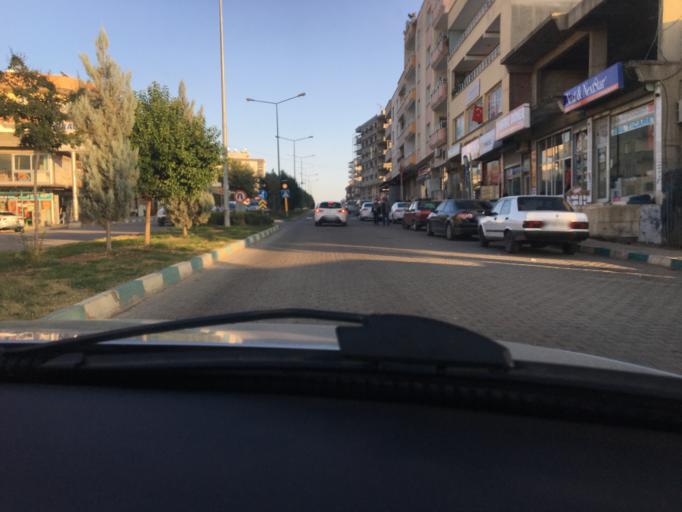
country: TR
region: Sanliurfa
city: Halfeti
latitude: 37.2318
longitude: 37.9426
